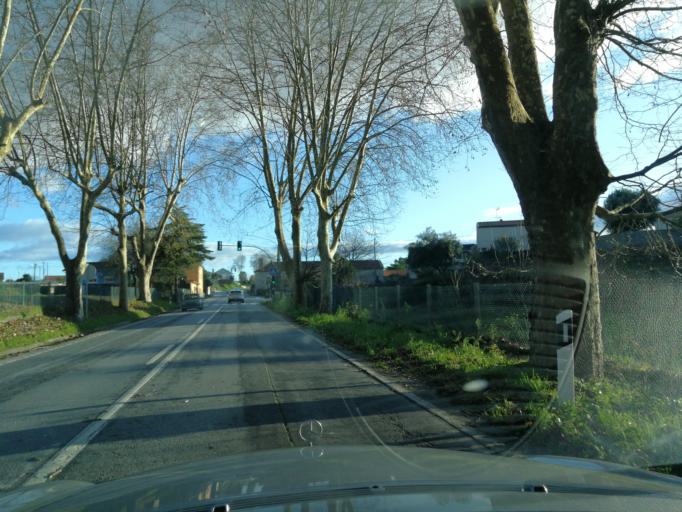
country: PT
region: Viana do Castelo
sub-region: Viana do Castelo
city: Darque
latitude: 41.6243
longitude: -8.7575
